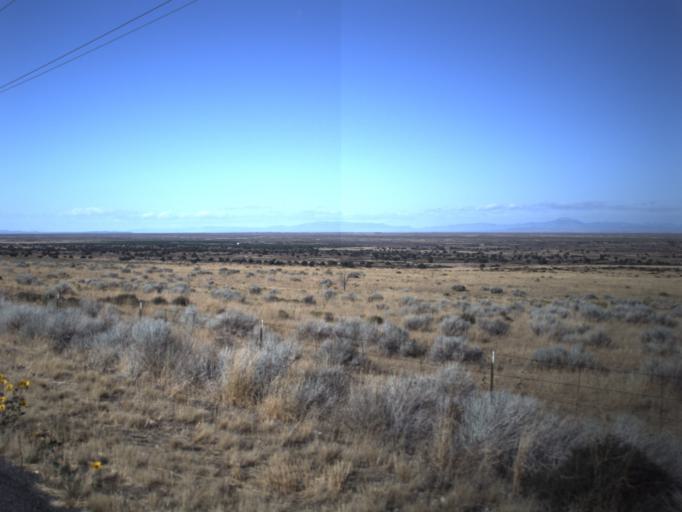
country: US
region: Utah
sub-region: Millard County
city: Delta
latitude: 39.4496
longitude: -112.3077
